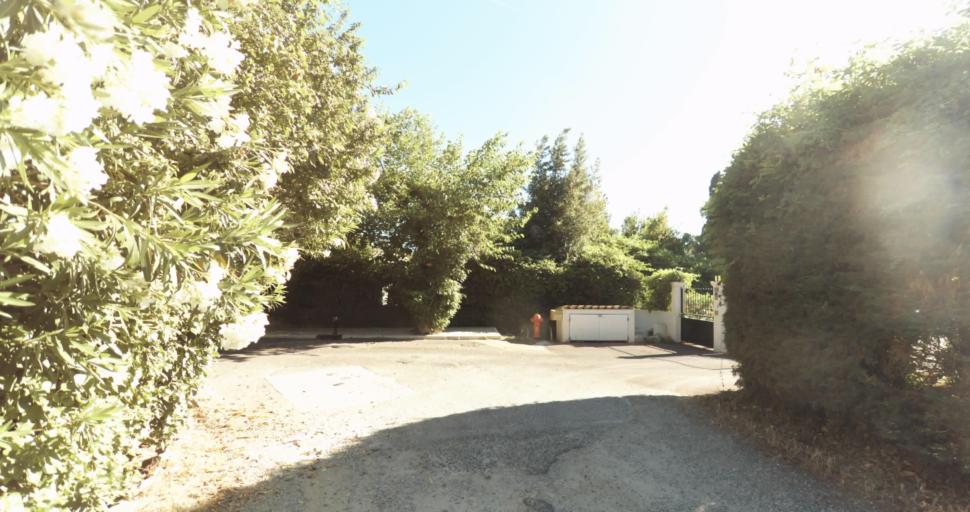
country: FR
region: Provence-Alpes-Cote d'Azur
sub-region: Departement du Var
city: Saint-Tropez
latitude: 43.2630
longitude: 6.6235
